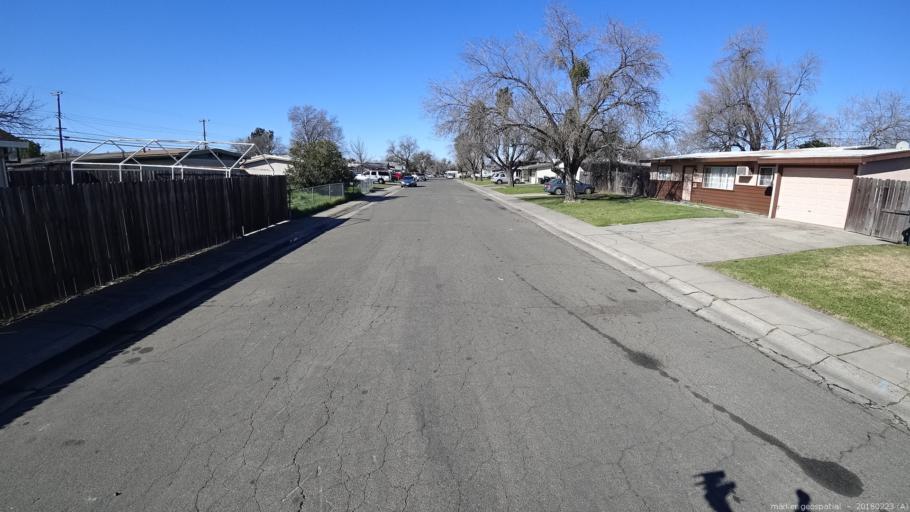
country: US
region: California
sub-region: Sacramento County
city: North Highlands
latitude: 38.7051
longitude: -121.3878
